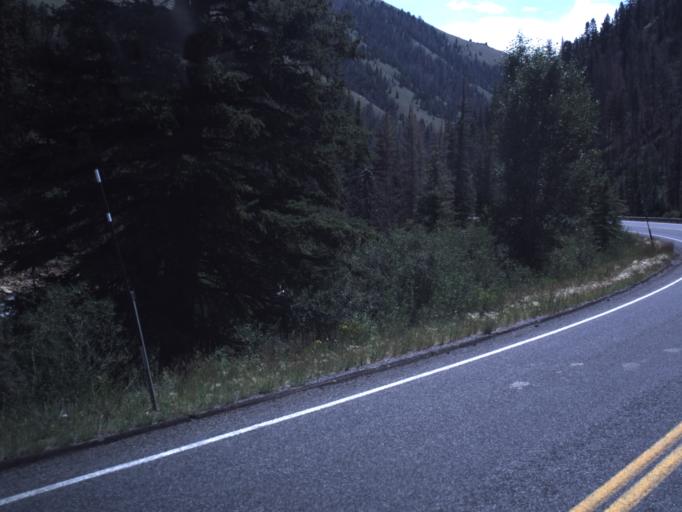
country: US
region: Utah
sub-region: Emery County
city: Huntington
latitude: 39.5018
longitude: -111.1593
